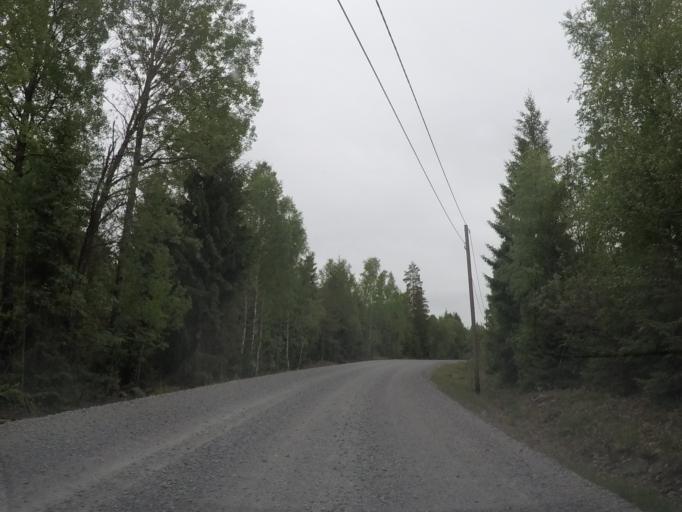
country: SE
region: Soedermanland
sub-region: Flens Kommun
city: Halleforsnas
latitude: 59.1797
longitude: 16.5024
